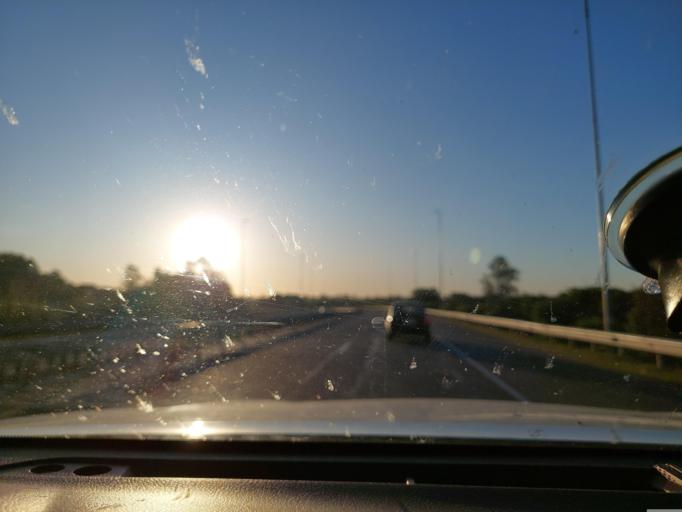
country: UY
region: Canelones
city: Pando
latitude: -34.7127
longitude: -55.9407
